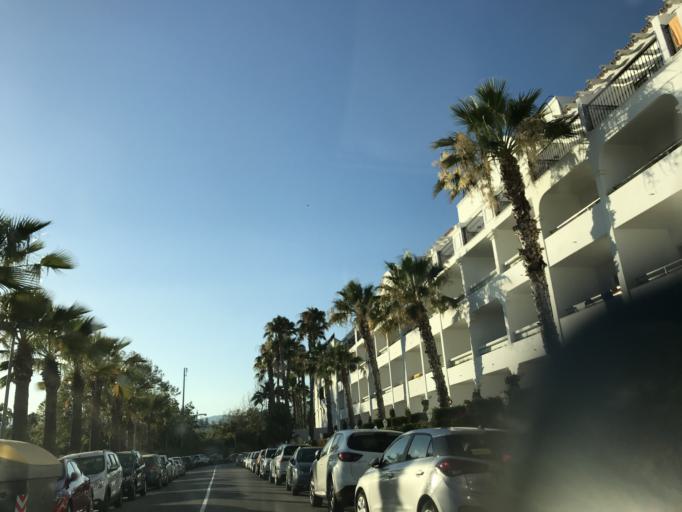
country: ES
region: Andalusia
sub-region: Provincia de Malaga
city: Benahavis
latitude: 36.4560
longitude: -5.0476
